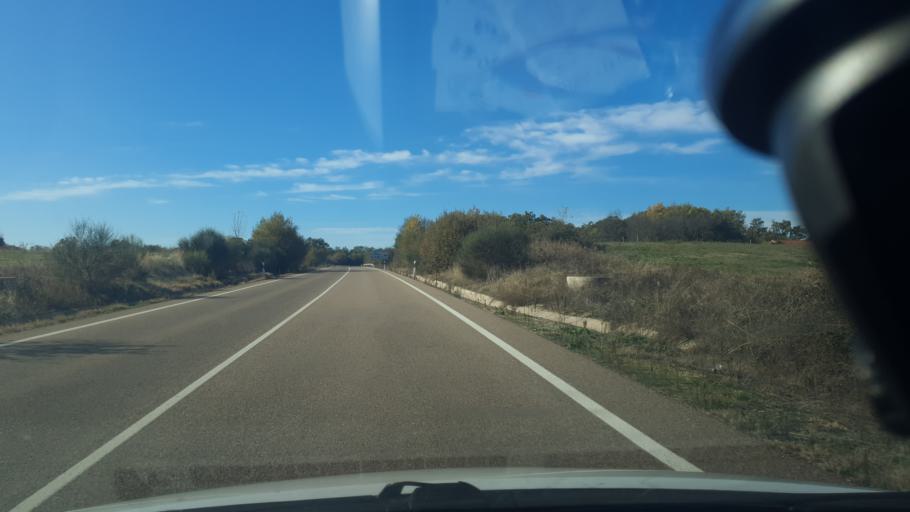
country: ES
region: Castille and Leon
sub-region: Provincia de Avila
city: Candeleda
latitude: 40.1366
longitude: -5.2203
